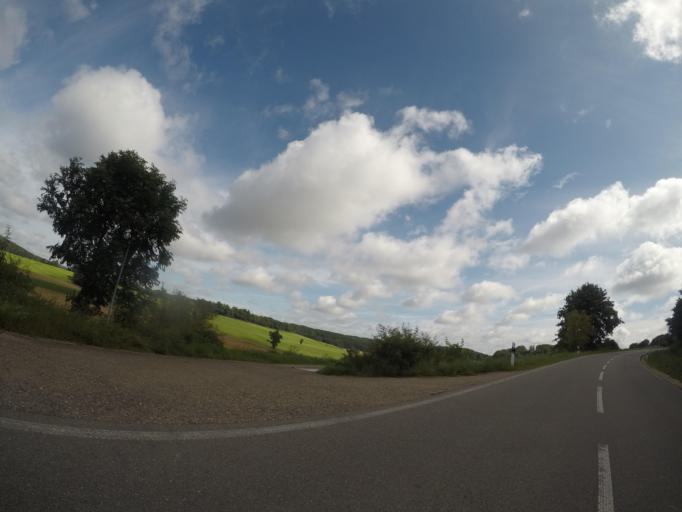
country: DE
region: Baden-Wuerttemberg
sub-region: Tuebingen Region
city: Laichingen
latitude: 48.4525
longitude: 9.6363
